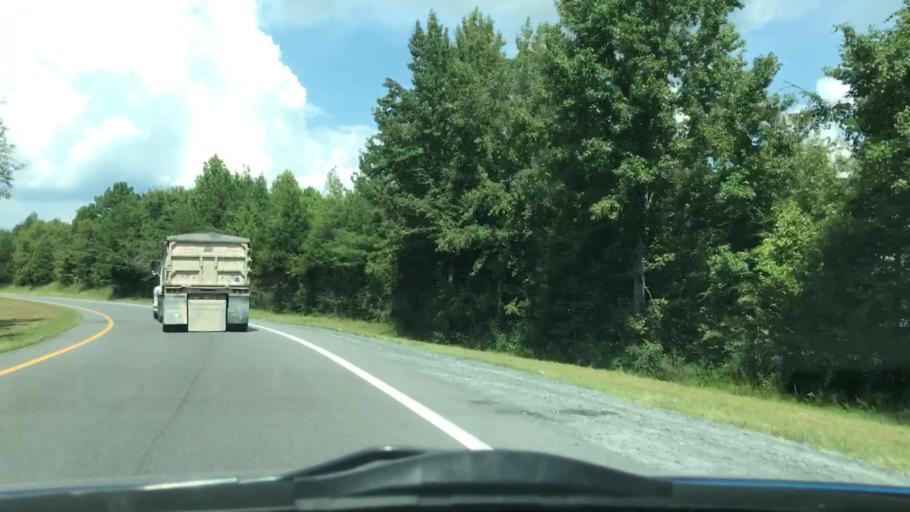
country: US
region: North Carolina
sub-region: Randolph County
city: Randleman
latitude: 35.8257
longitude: -79.8243
